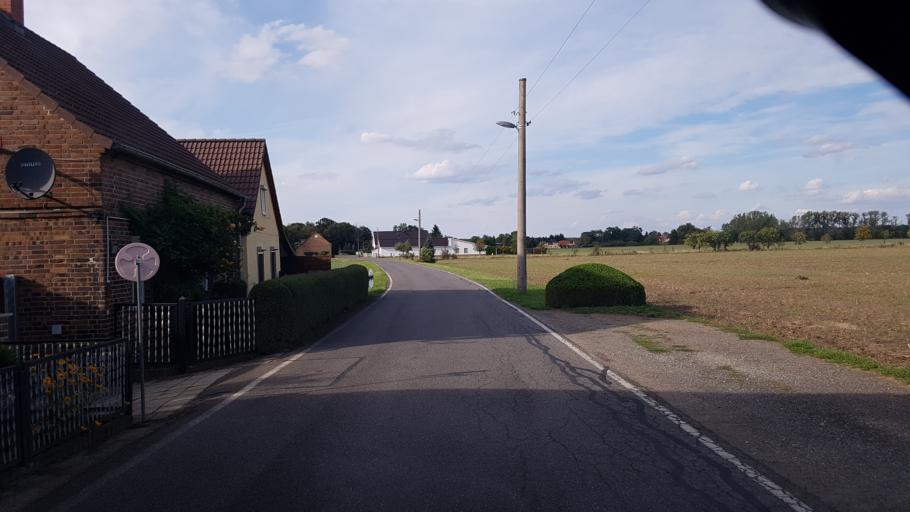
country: DE
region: Brandenburg
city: Welzow
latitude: 51.5723
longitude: 14.1108
